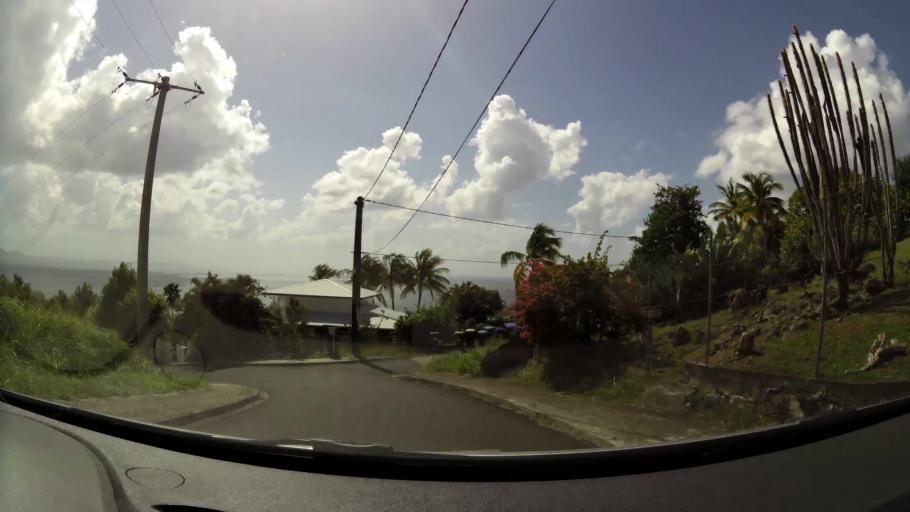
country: MQ
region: Martinique
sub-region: Martinique
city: Fort-de-France
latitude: 14.6359
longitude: -61.1263
